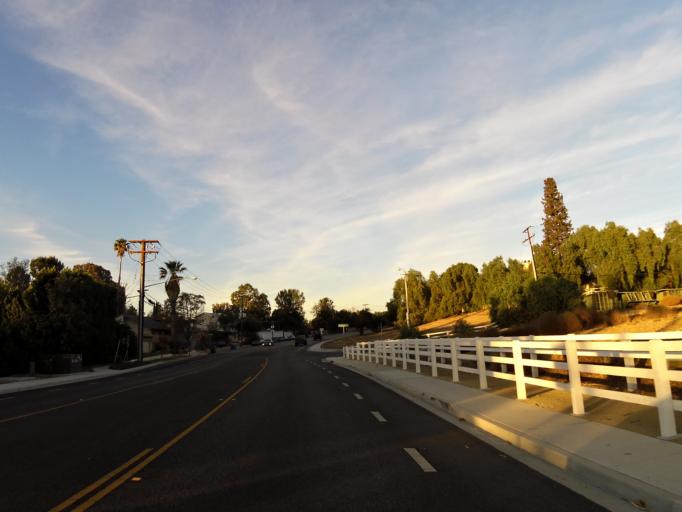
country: US
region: California
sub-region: Ventura County
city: Thousand Oaks
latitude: 34.1871
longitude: -118.8472
